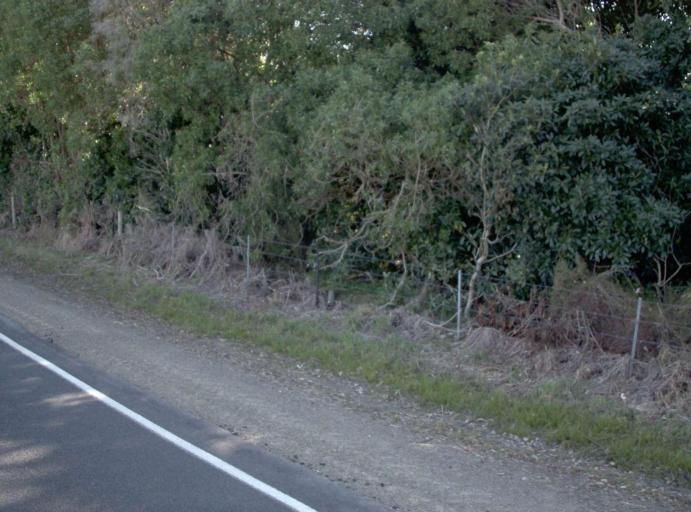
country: AU
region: Victoria
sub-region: East Gippsland
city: Lakes Entrance
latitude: -37.7346
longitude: 148.5049
